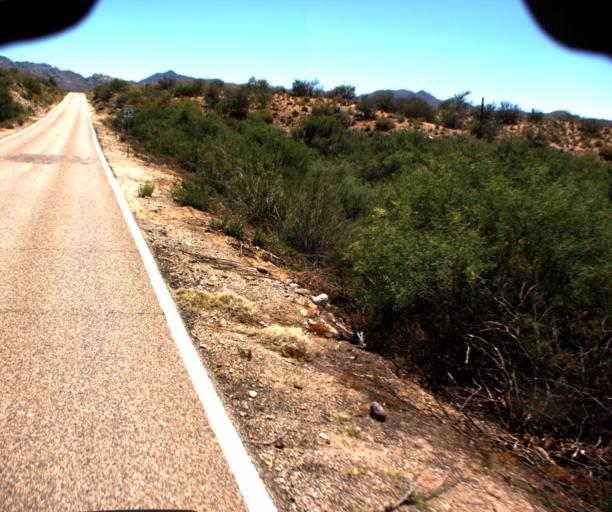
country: US
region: Arizona
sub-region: Yavapai County
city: Bagdad
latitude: 34.4793
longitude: -113.0592
